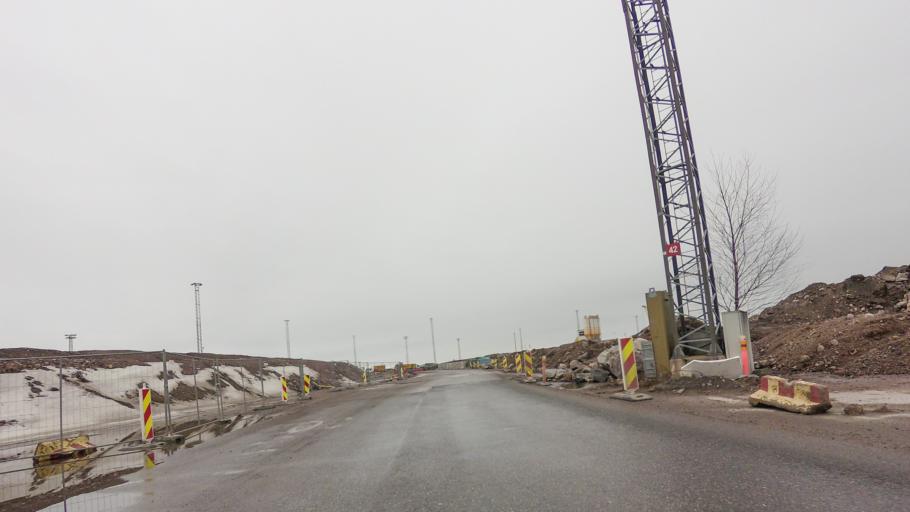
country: FI
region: Uusimaa
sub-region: Helsinki
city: Helsinki
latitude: 60.1541
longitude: 24.9126
